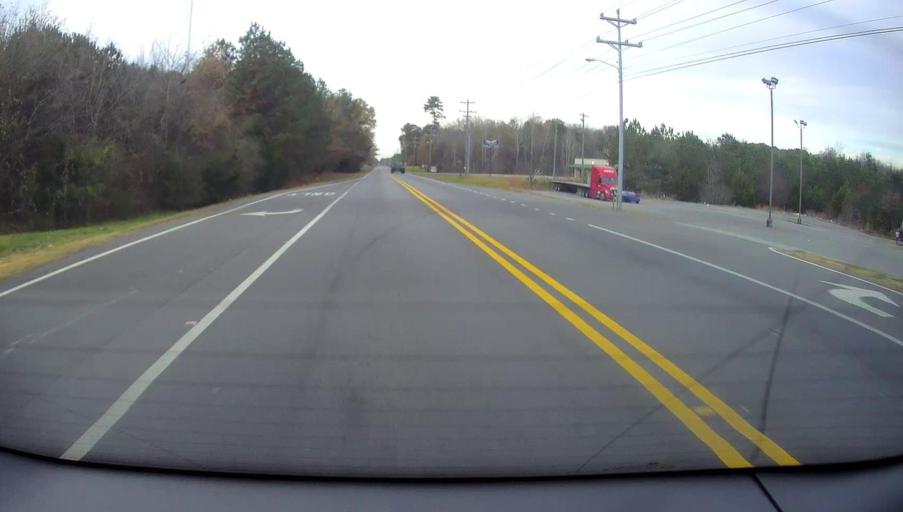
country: US
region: Alabama
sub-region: Morgan County
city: Priceville
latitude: 34.4473
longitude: -86.7581
